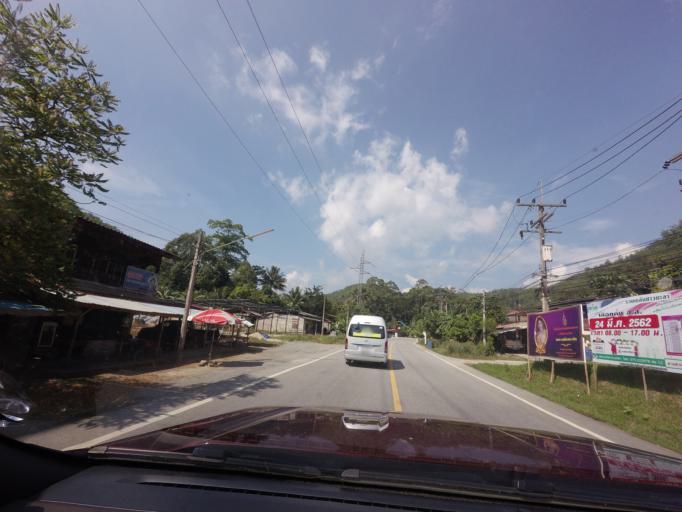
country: TH
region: Yala
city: Betong
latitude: 5.9370
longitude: 101.1868
